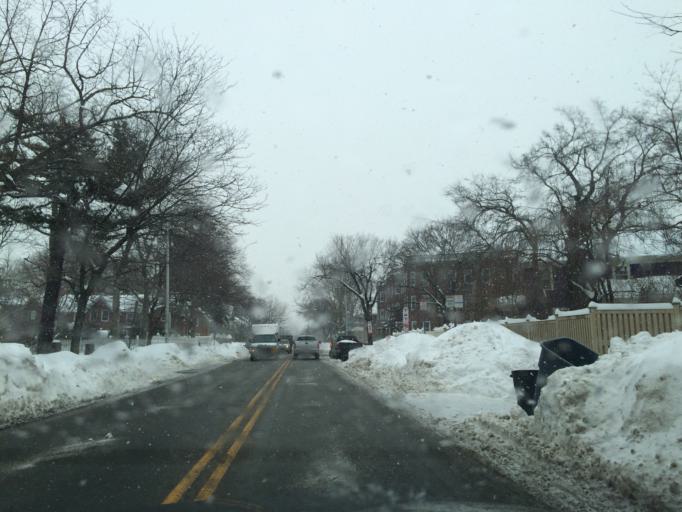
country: US
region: Massachusetts
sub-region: Middlesex County
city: Cambridge
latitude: 42.3775
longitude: -71.1102
